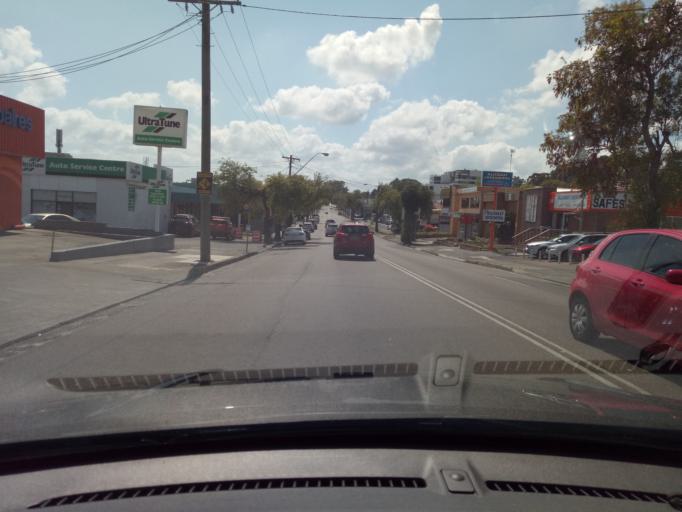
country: AU
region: New South Wales
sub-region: Gosford Shire
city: Gosford
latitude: -33.4188
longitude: 151.3435
